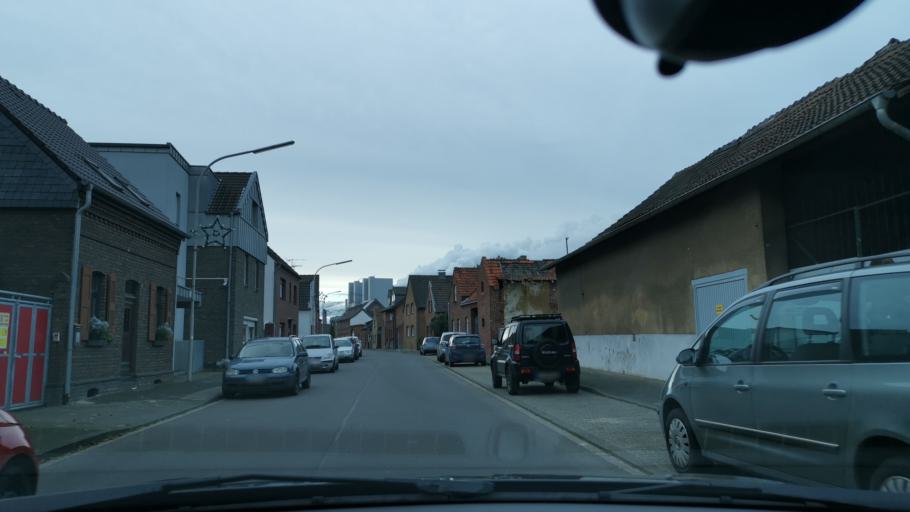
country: DE
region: North Rhine-Westphalia
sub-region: Regierungsbezirk Dusseldorf
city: Rommerskirchen
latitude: 51.0293
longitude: 6.6612
